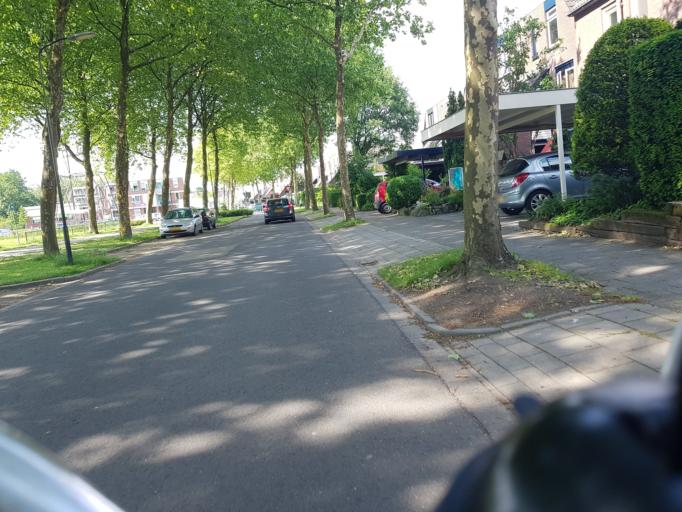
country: NL
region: Gelderland
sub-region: Gemeente Apeldoorn
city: Apeldoorn
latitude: 52.1870
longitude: 6.0016
